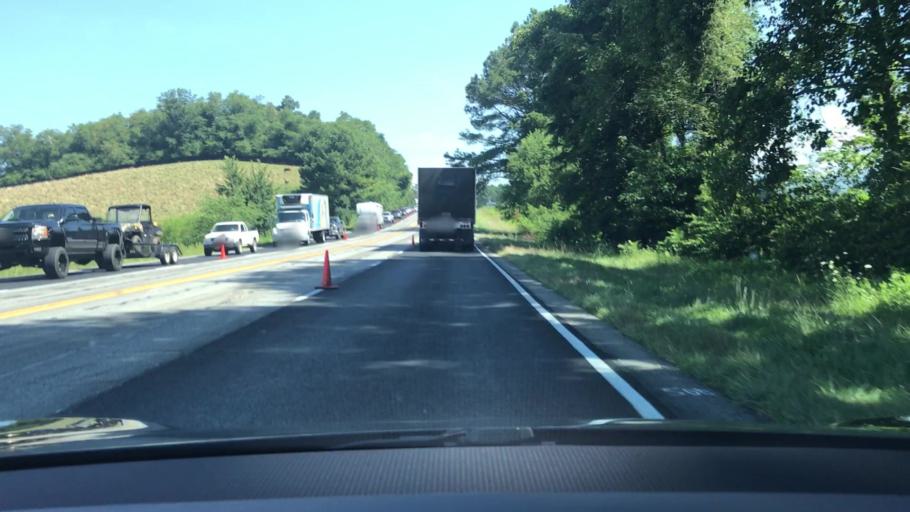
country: US
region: Georgia
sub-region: Rabun County
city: Mountain City
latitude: 34.9517
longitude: -83.3865
